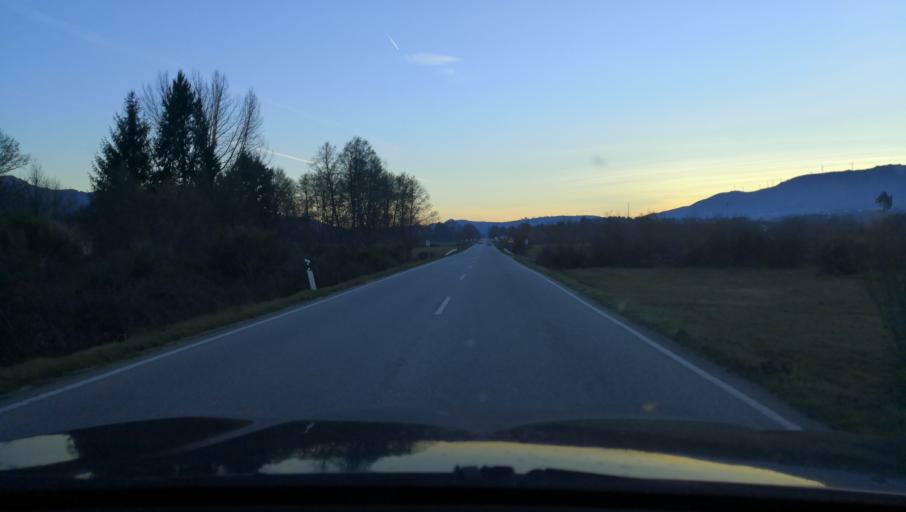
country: PT
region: Vila Real
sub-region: Vila Pouca de Aguiar
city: Vila Pouca de Aguiar
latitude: 41.4446
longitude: -7.6730
